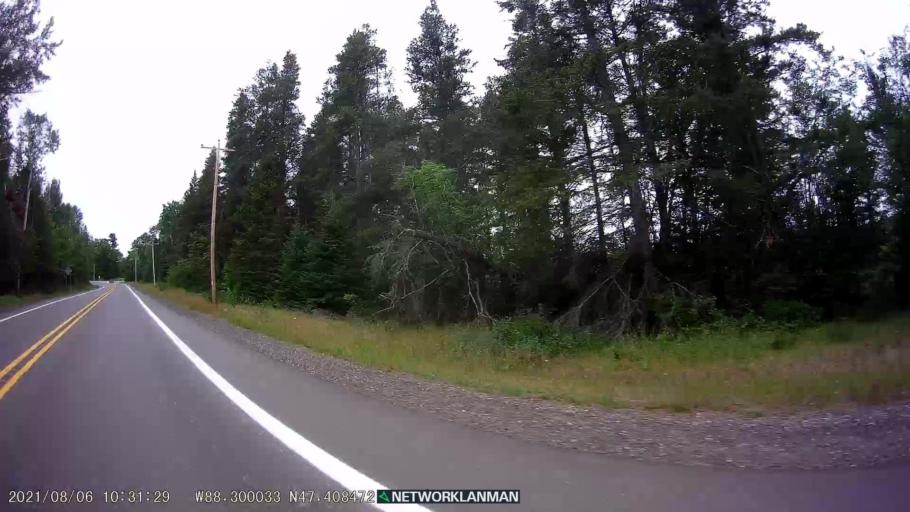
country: US
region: Michigan
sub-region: Keweenaw County
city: Eagle River
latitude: 47.4081
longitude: -88.2999
